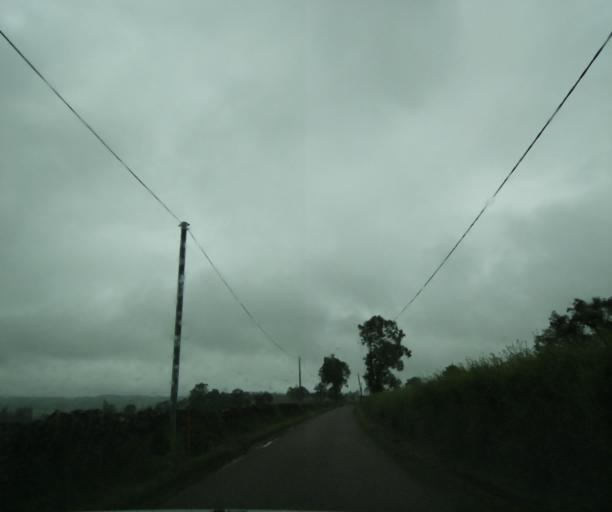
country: FR
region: Bourgogne
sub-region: Departement de Saone-et-Loire
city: Charolles
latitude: 46.3697
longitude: 4.2113
